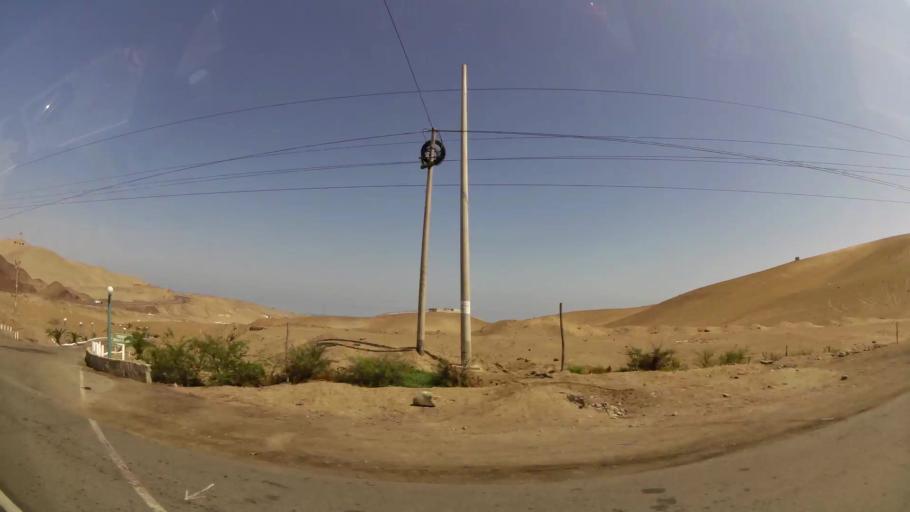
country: PE
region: Lima
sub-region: Provincia de Canete
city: Quilmana
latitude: -12.9377
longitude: -76.4970
